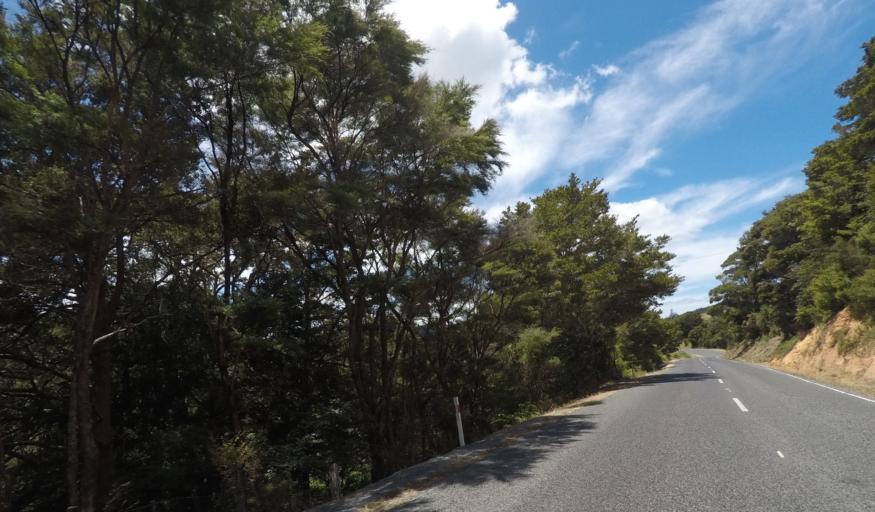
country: NZ
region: Northland
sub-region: Whangarei
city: Ngunguru
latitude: -35.5079
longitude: 174.4187
